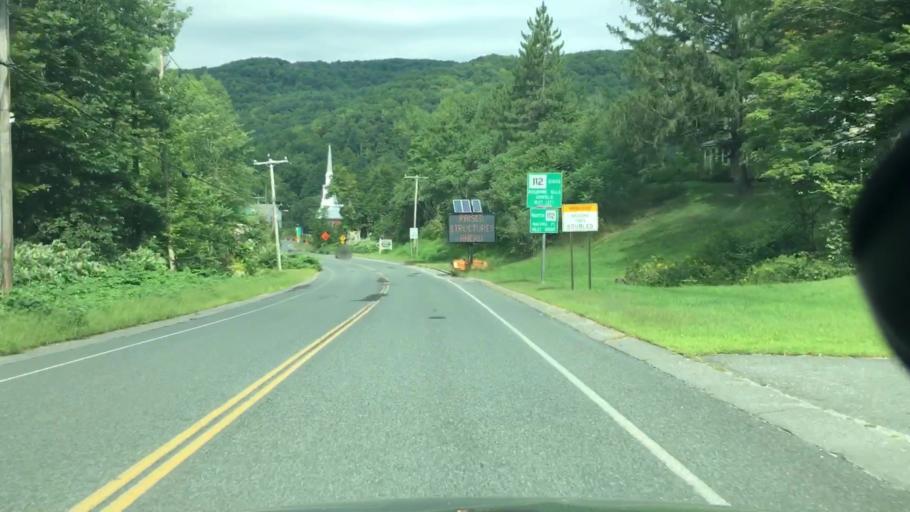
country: US
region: Massachusetts
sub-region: Franklin County
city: Colrain
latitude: 42.6709
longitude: -72.6947
